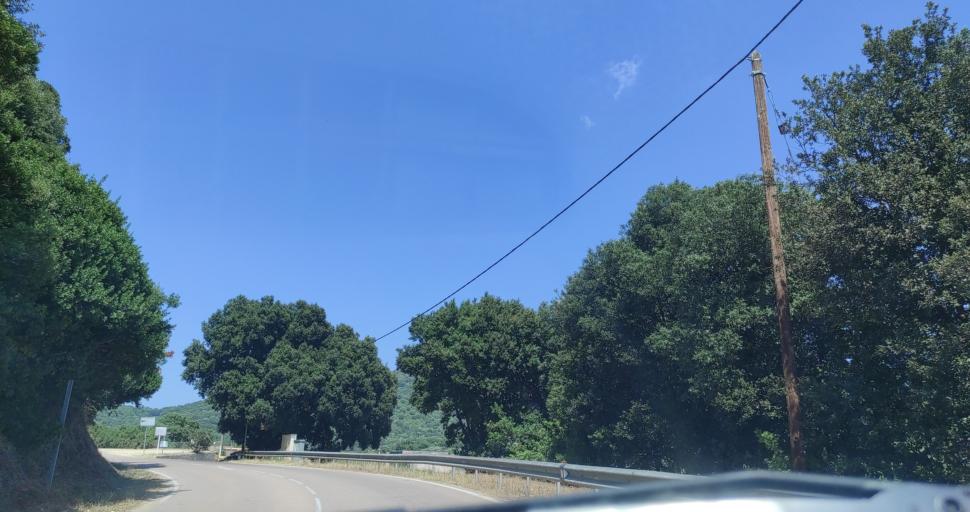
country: FR
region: Corsica
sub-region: Departement de la Corse-du-Sud
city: Alata
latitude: 41.9609
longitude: 8.7274
